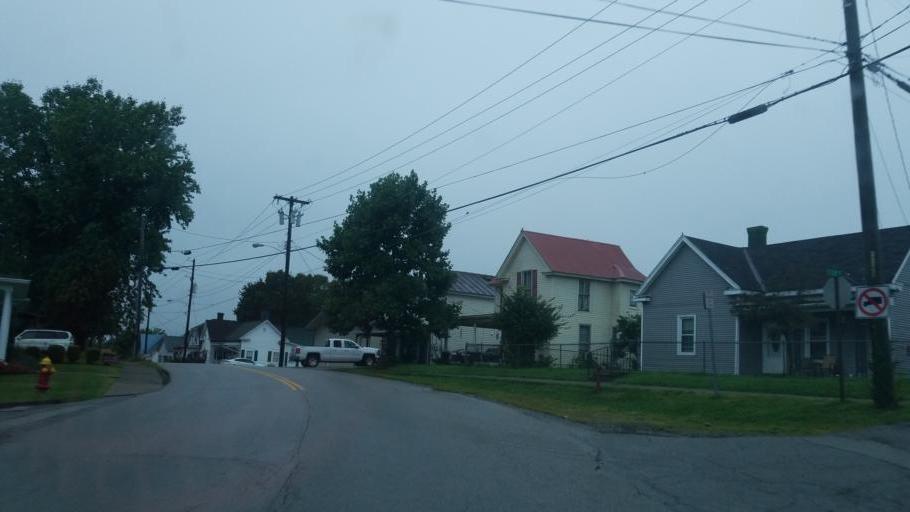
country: US
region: Kentucky
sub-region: Fleming County
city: Flemingsburg
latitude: 38.4229
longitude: -83.7295
